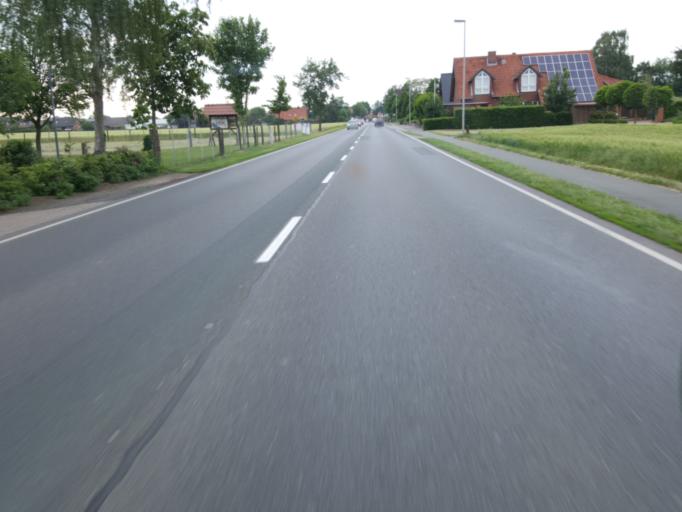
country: DE
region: Lower Saxony
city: Leese
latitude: 52.4964
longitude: 9.1207
